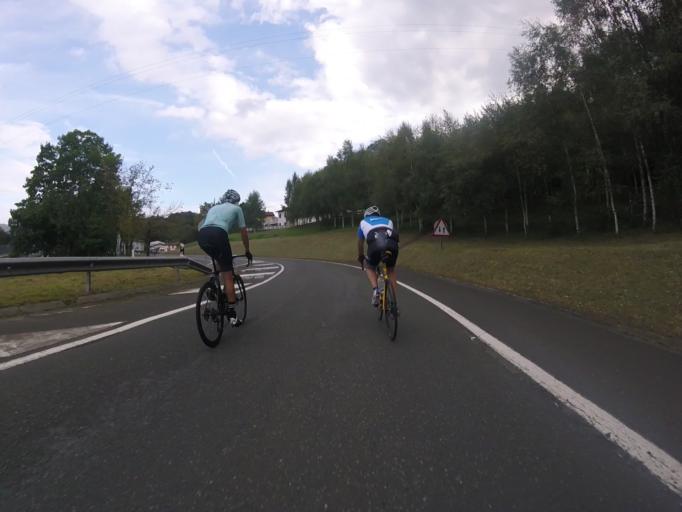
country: ES
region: Basque Country
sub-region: Provincia de Guipuzcoa
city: Villabona
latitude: 43.1838
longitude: -2.0511
